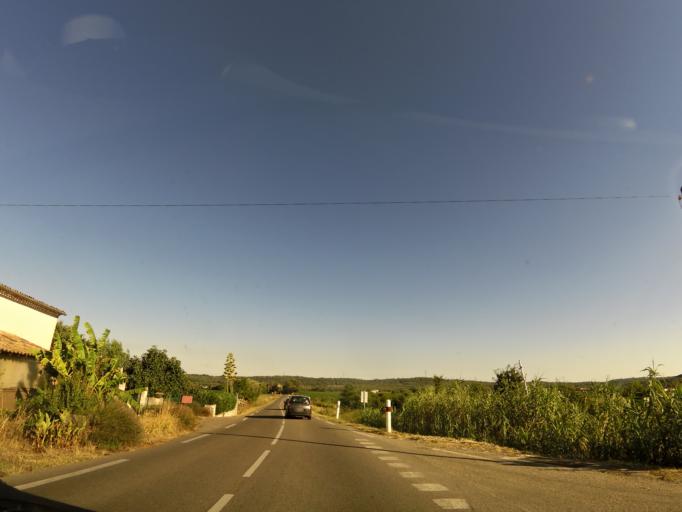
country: FR
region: Languedoc-Roussillon
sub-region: Departement du Gard
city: Quissac
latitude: 43.8399
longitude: 4.0292
